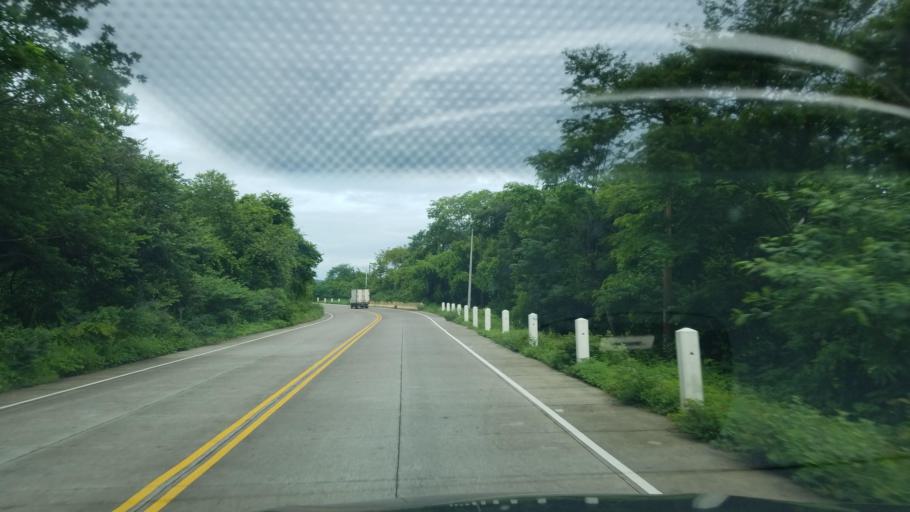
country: HN
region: Francisco Morazan
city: El Porvenir
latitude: 13.6848
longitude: -87.3550
